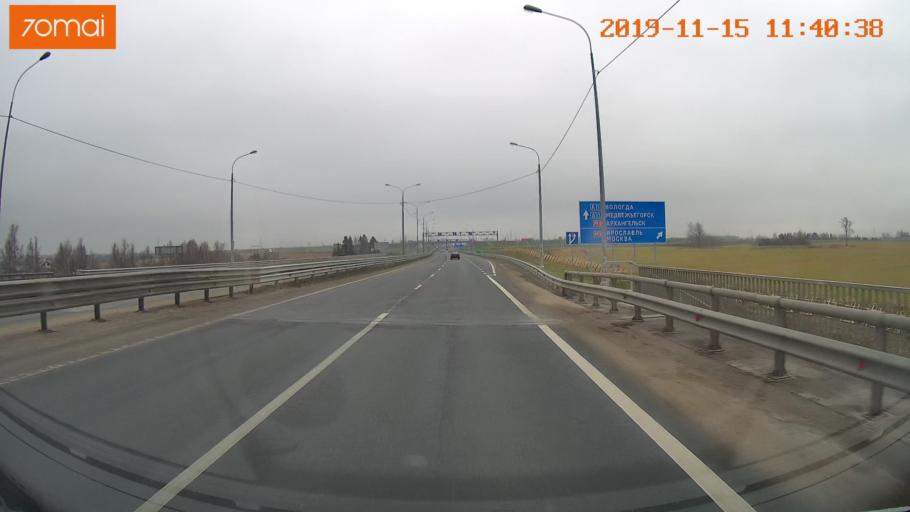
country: RU
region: Vologda
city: Molochnoye
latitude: 59.2127
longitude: 39.7557
